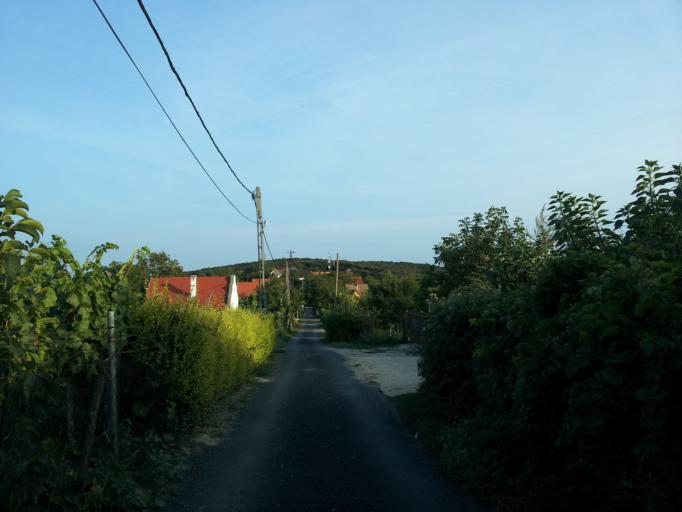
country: HU
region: Somogy
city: Zamardi
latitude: 46.8709
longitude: 17.9334
